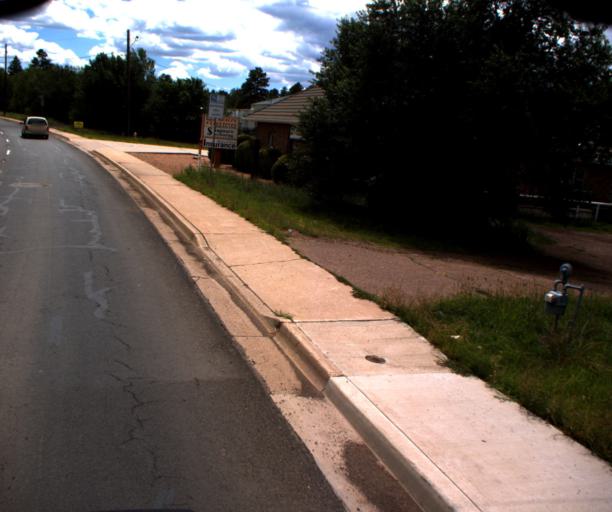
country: US
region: Arizona
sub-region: Navajo County
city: Show Low
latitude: 34.2496
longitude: -110.0287
